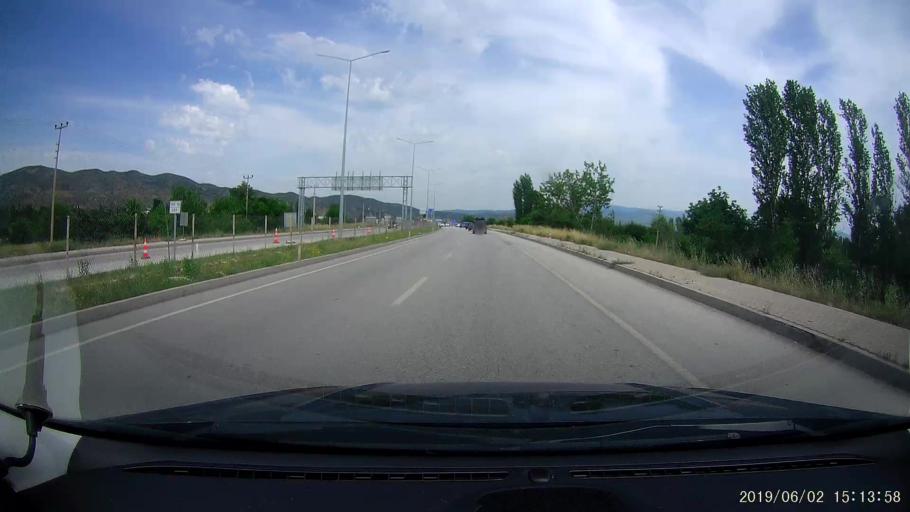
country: TR
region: Corum
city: Osmancik
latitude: 40.9704
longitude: 34.8291
